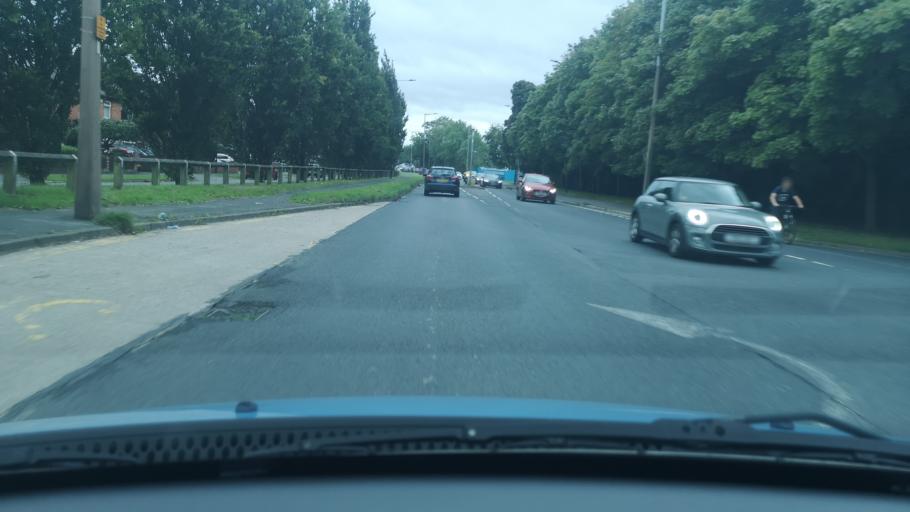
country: GB
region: England
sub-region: Doncaster
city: Kirk Sandall
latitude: 53.5515
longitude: -1.0850
